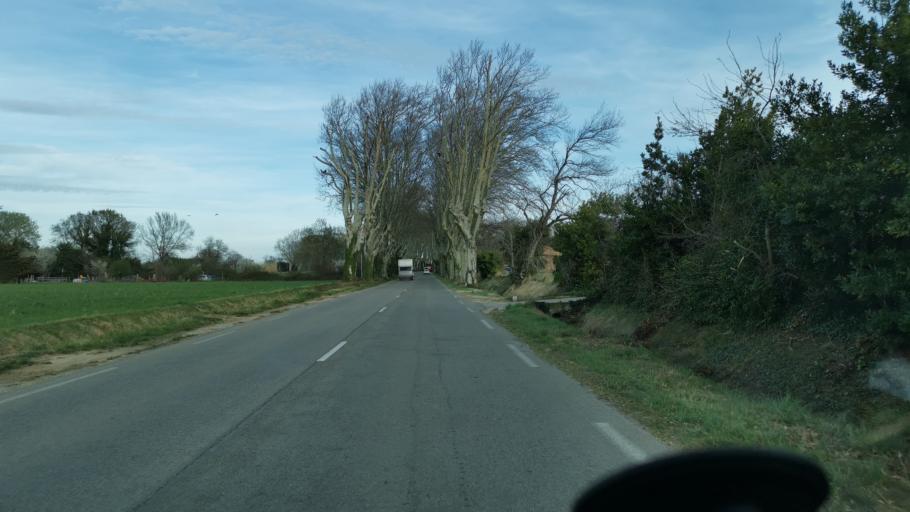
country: FR
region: Provence-Alpes-Cote d'Azur
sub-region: Departement des Bouches-du-Rhone
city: Saint-Martin-de-Crau
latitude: 43.6357
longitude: 4.7566
